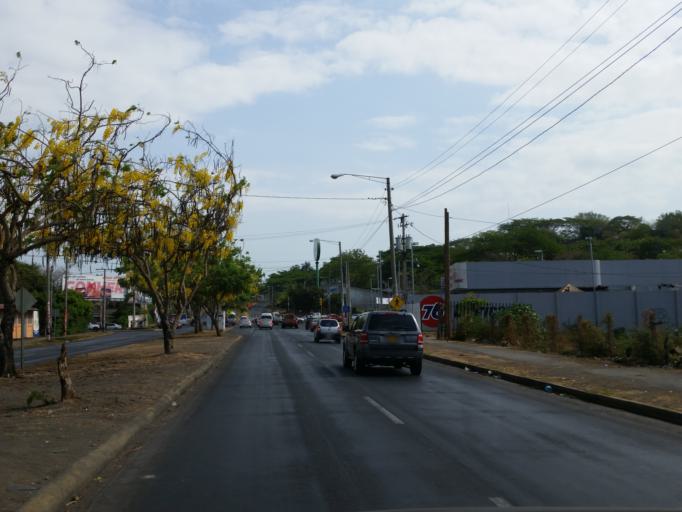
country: NI
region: Managua
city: Managua
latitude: 12.1352
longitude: -86.2751
